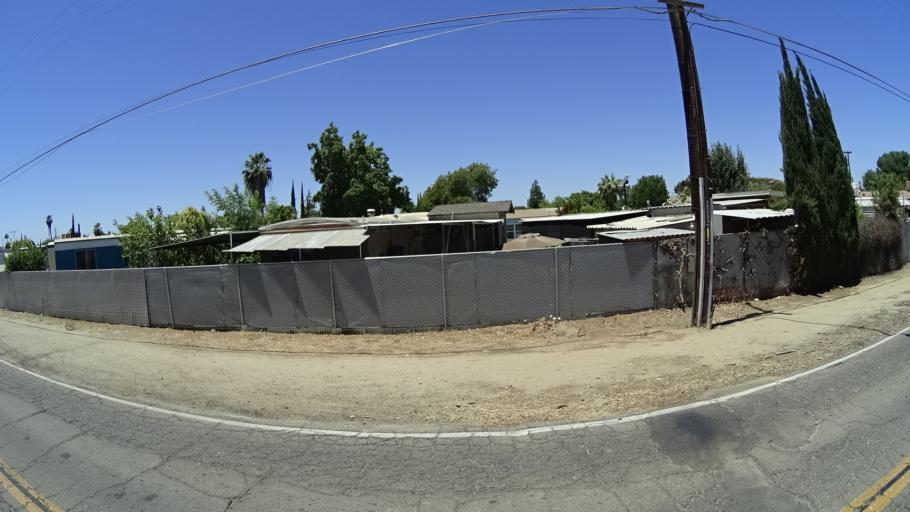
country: US
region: California
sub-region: Fresno County
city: West Park
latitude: 36.7808
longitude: -119.8534
